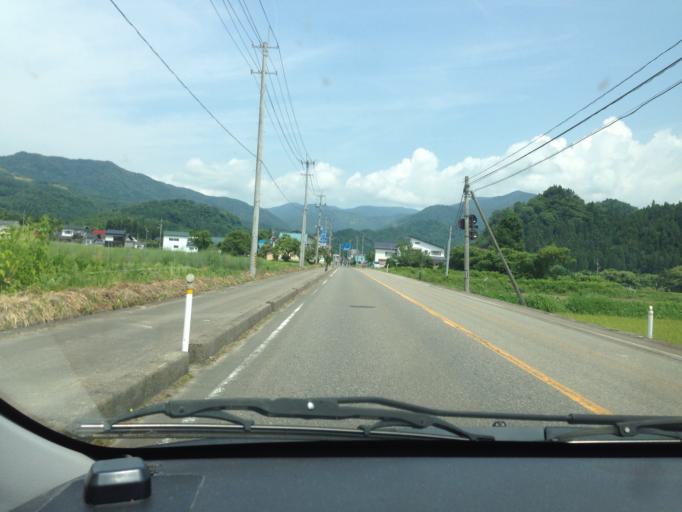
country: JP
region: Fukushima
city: Kitakata
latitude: 37.7215
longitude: 139.8804
